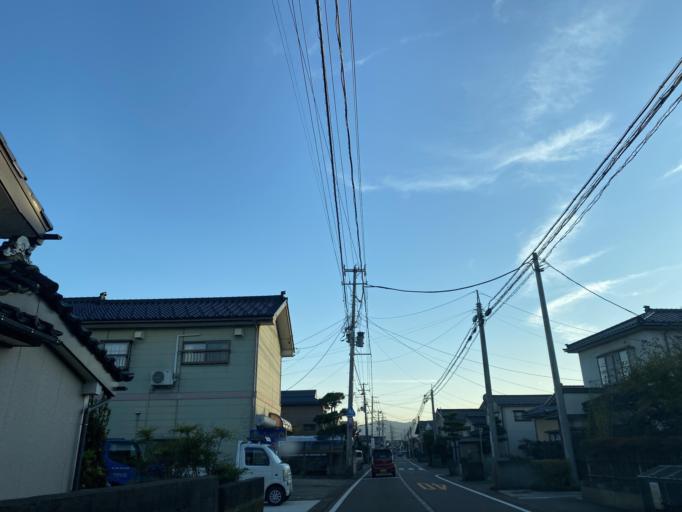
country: JP
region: Niigata
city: Kashiwazaki
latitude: 37.3826
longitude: 138.5685
